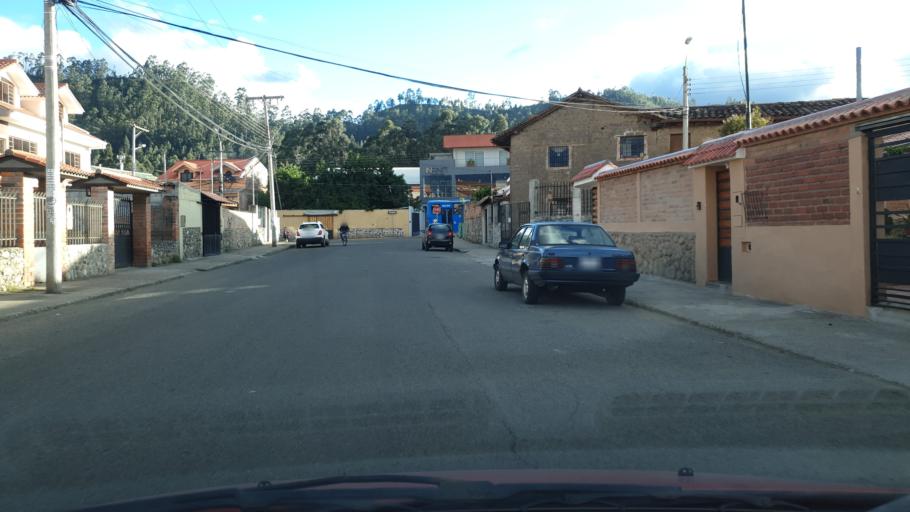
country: EC
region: Azuay
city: Cuenca
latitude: -2.9147
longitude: -79.0146
